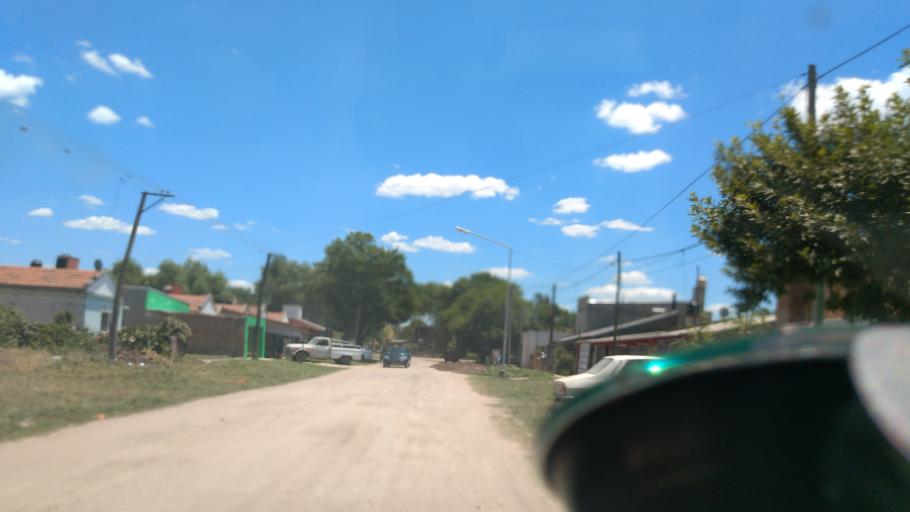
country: AR
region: Santa Fe
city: Laguna Paiva
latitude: -31.3117
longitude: -60.6610
